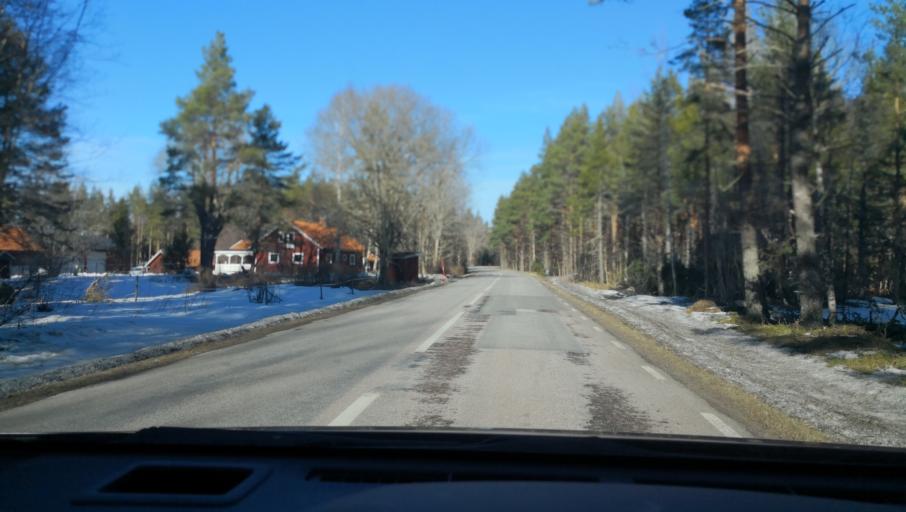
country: SE
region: Uppsala
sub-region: Osthammars Kommun
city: Osterbybruk
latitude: 60.2705
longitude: 17.9573
